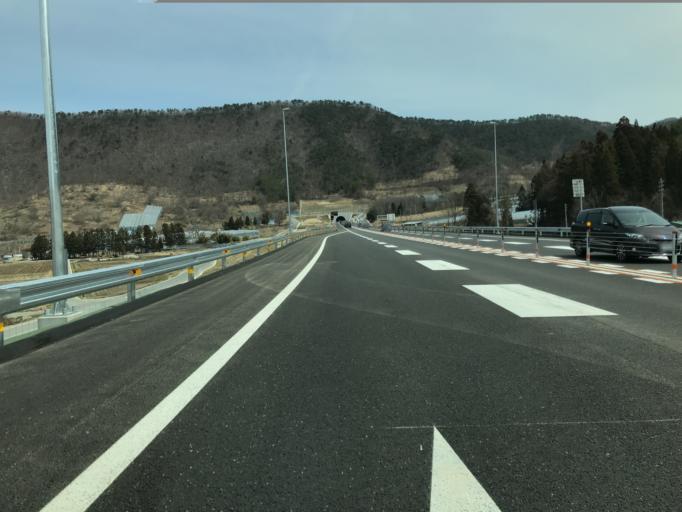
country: JP
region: Yamagata
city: Takahata
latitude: 38.0767
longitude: 140.1953
